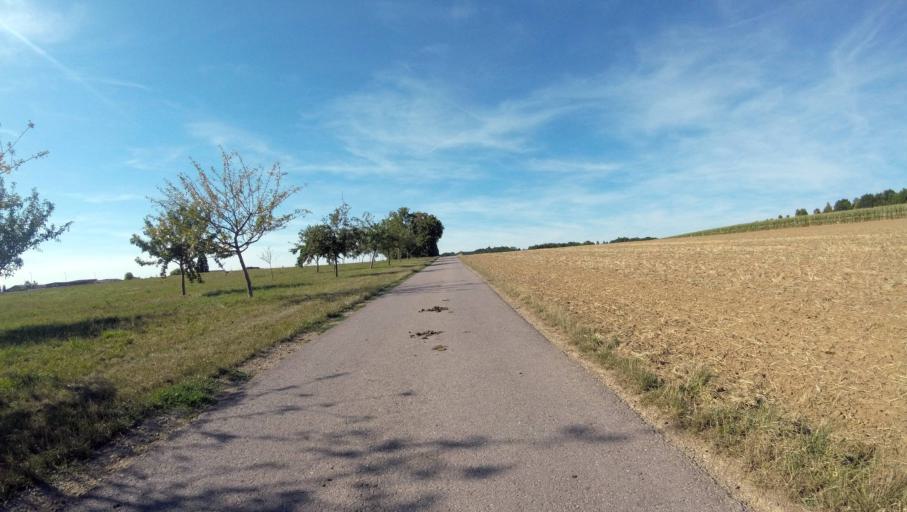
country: DE
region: Baden-Wuerttemberg
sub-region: Regierungsbezirk Stuttgart
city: Kirchberg an der Murr
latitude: 48.9516
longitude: 9.3454
